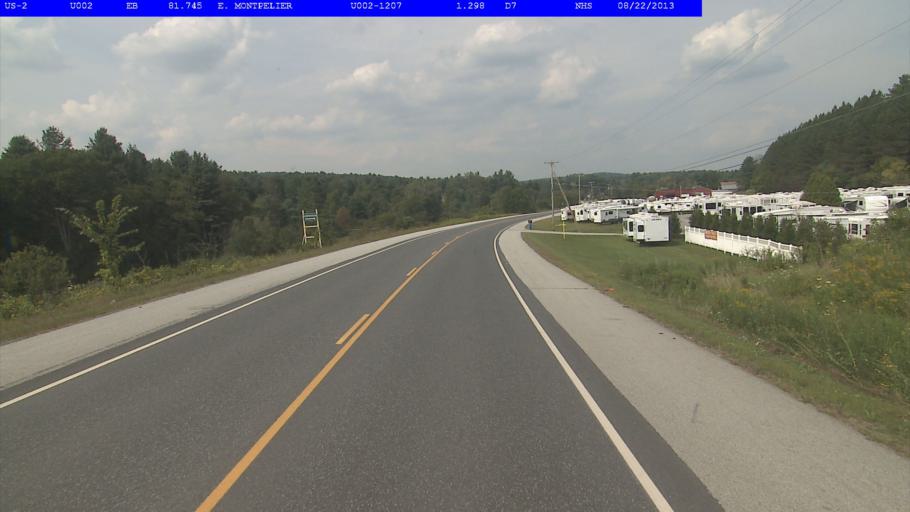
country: US
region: Vermont
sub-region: Washington County
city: Barre
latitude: 44.2518
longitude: -72.5018
